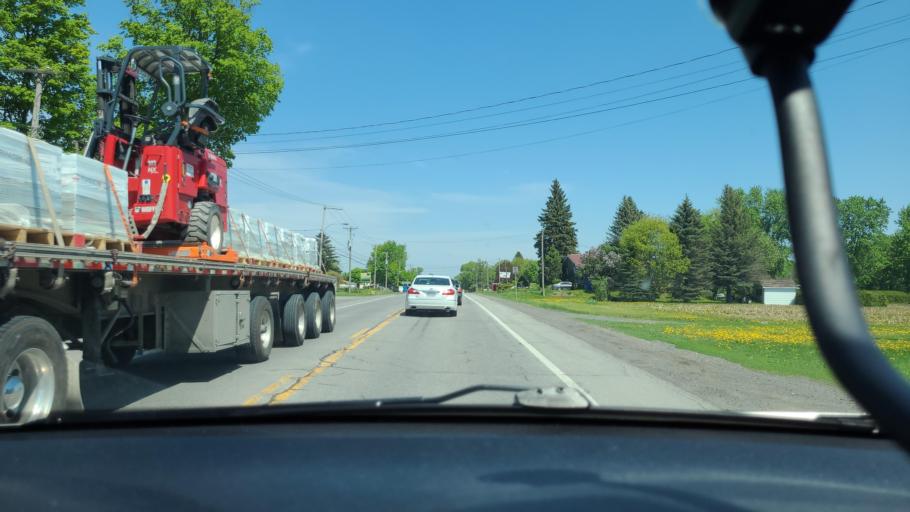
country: CA
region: Quebec
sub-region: Laurentides
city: Saint-Eustache
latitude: 45.5835
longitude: -73.9566
